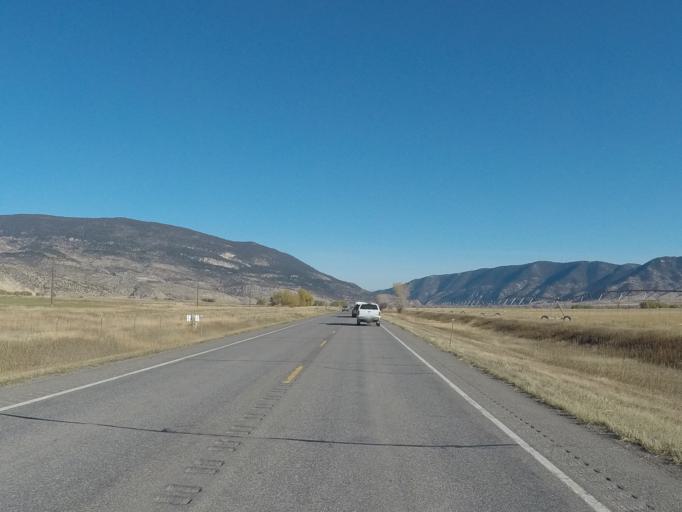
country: US
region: Montana
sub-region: Park County
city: Livingston
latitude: 45.5375
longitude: -110.6026
